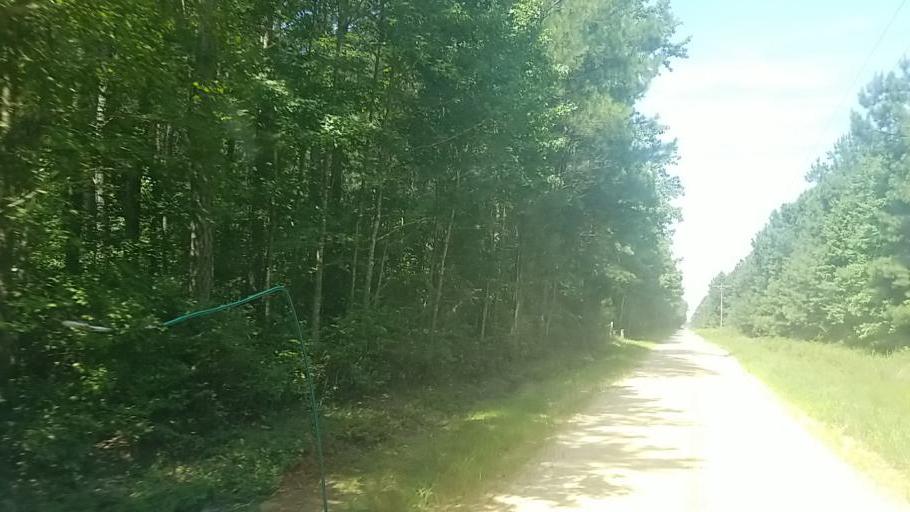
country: US
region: Maryland
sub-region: Caroline County
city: Denton
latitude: 38.8682
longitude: -75.7355
